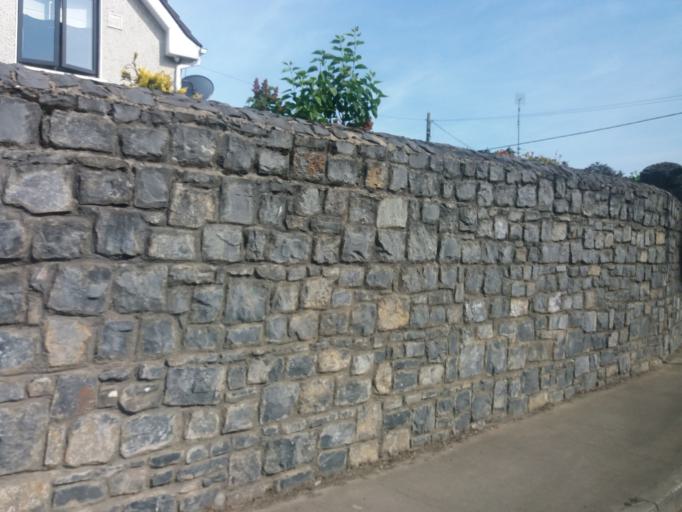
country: IE
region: Leinster
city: Lusk
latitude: 53.5267
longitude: -6.1698
